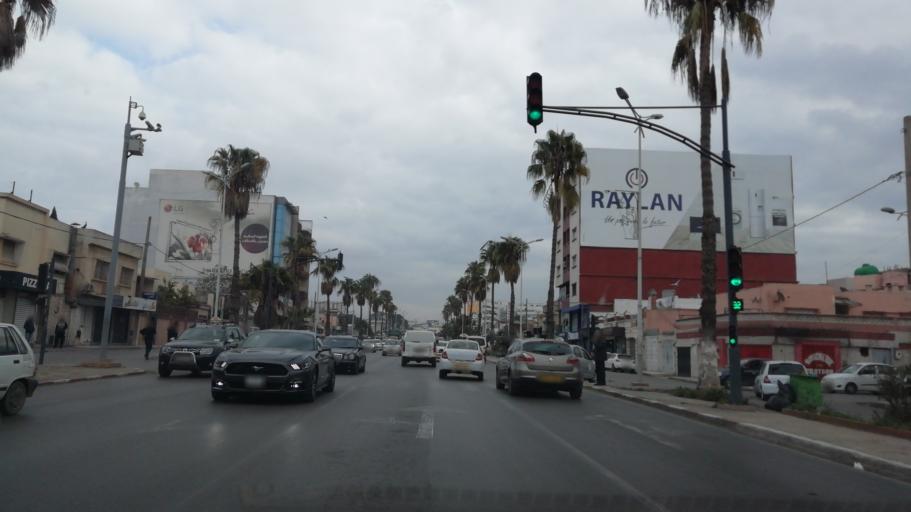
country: DZ
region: Oran
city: Oran
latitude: 35.6944
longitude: -0.6162
